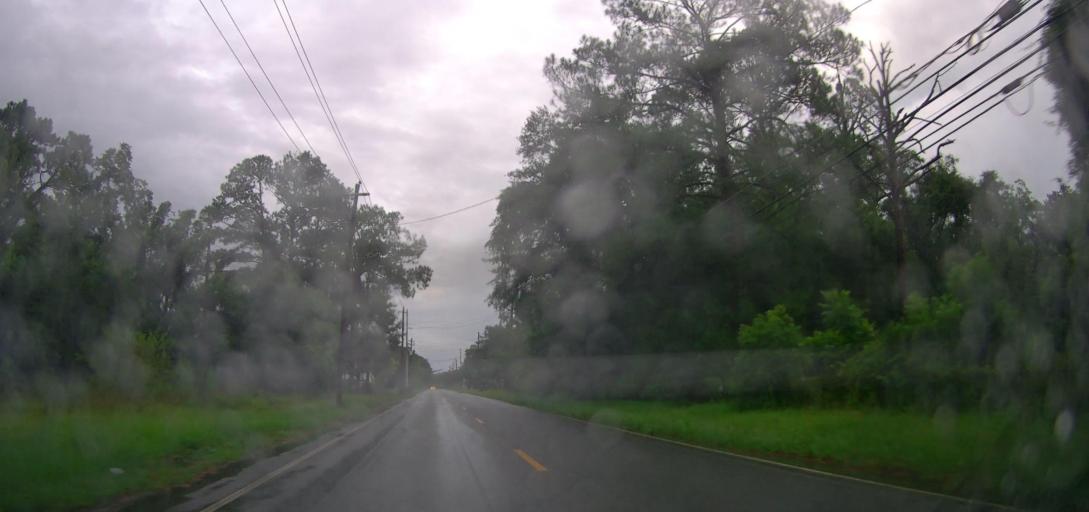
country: US
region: Georgia
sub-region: Ware County
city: Waycross
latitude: 31.2004
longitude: -82.3728
